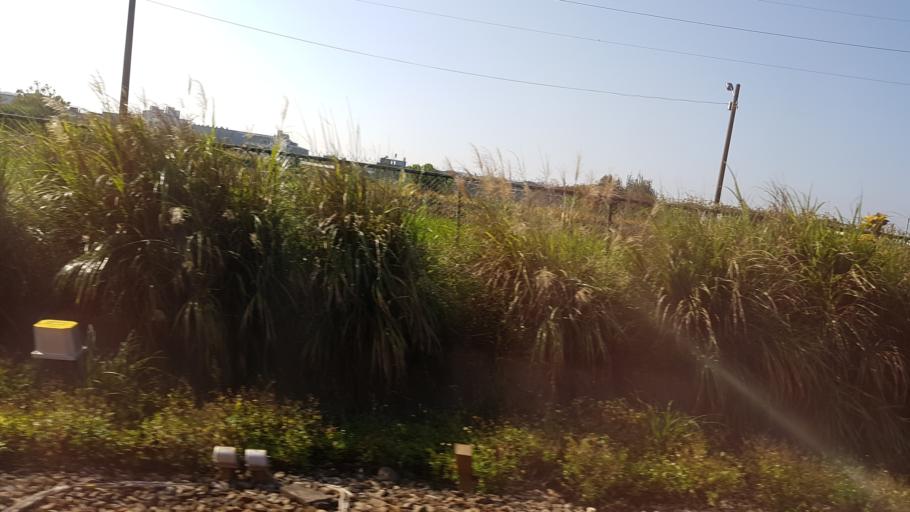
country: TW
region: Taiwan
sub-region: Miaoli
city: Miaoli
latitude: 24.6572
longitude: 120.8767
